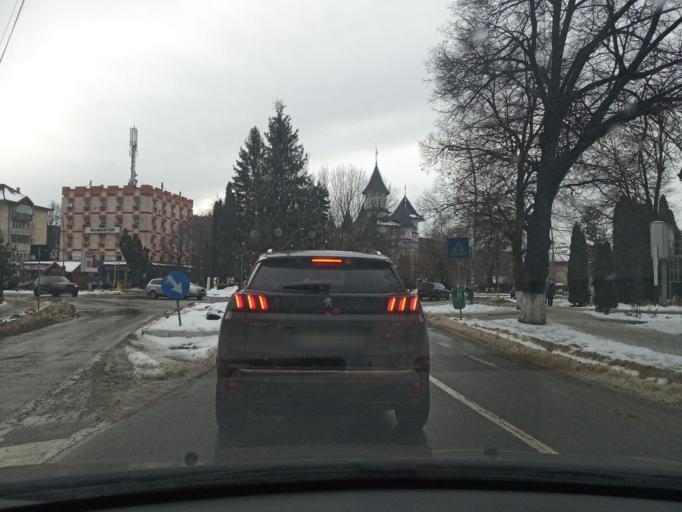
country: RO
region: Suceava
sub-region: Oras Gura Humorului
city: Gura Humorului
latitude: 47.5552
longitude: 25.8905
